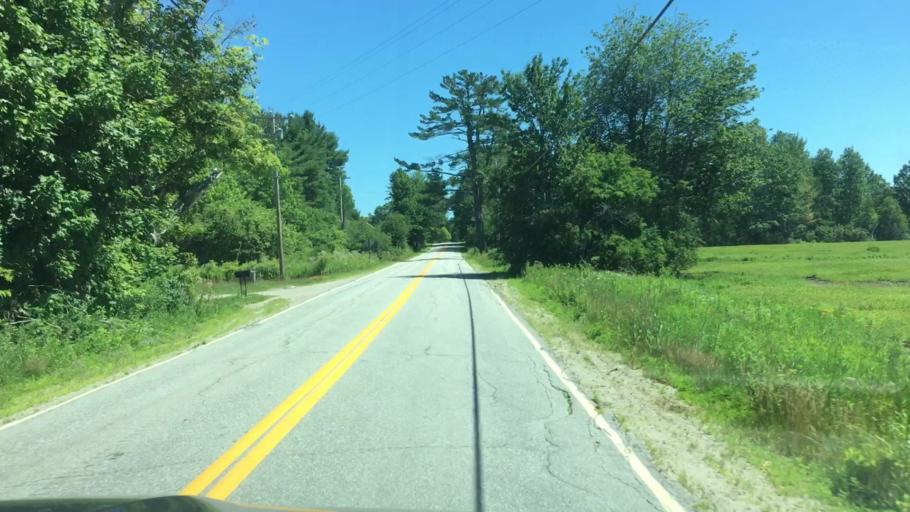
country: US
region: Maine
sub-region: Hancock County
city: Penobscot
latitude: 44.5175
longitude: -68.6689
